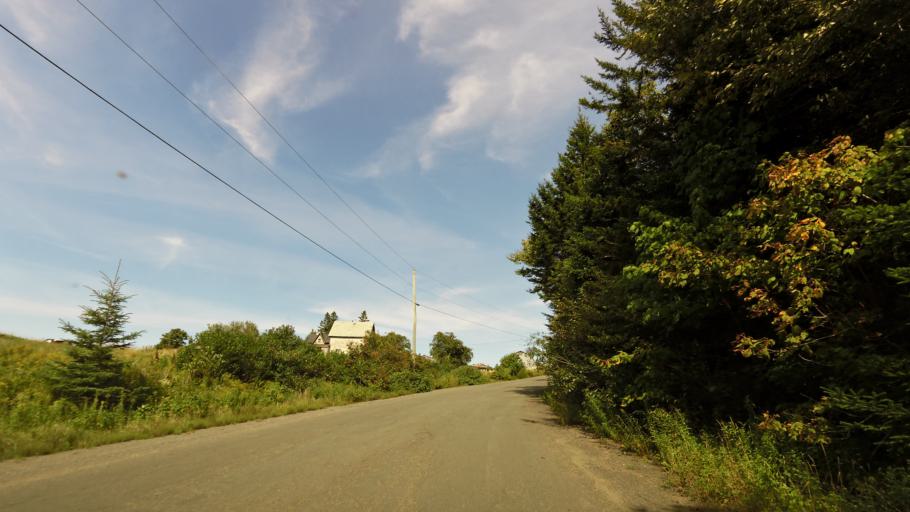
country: CA
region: New Brunswick
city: Hampton
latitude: 45.5635
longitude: -65.8436
